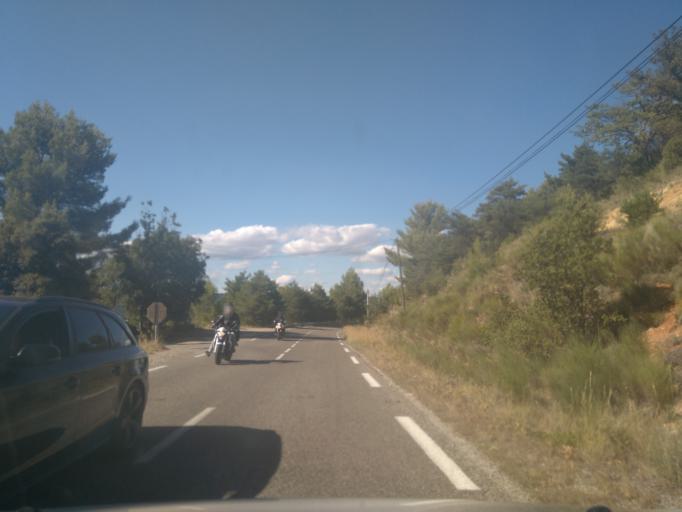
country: FR
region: Provence-Alpes-Cote d'Azur
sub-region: Departement du Var
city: Regusse
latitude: 43.7310
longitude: 6.1595
